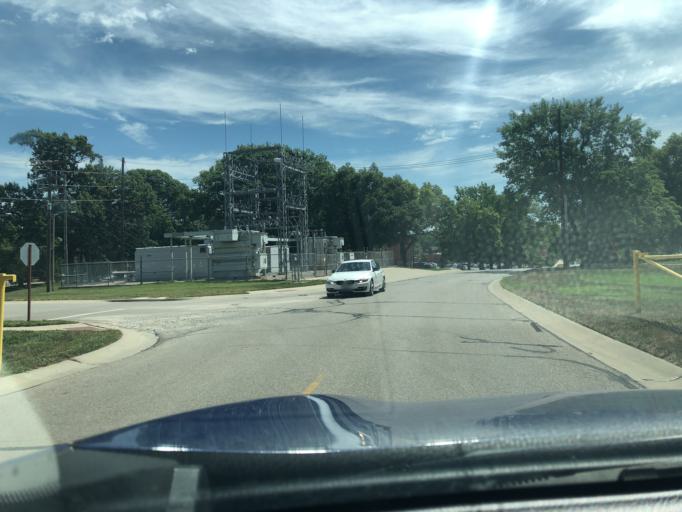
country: US
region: Kansas
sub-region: Leavenworth County
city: Leavenworth
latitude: 39.3531
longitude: -94.9281
